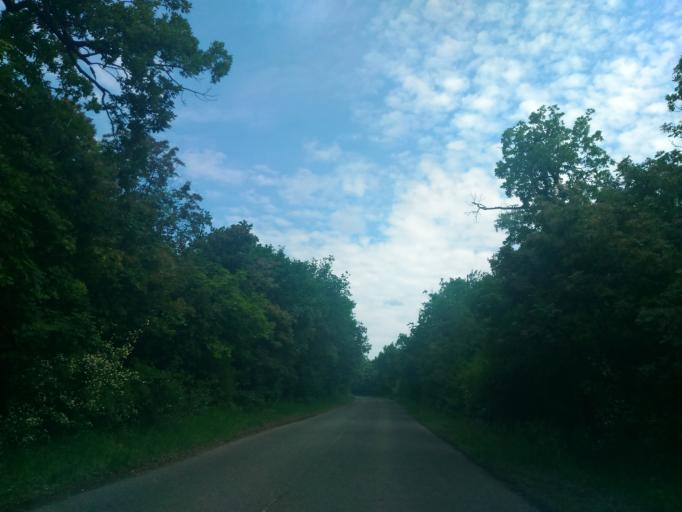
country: HU
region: Baranya
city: Pecs
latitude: 46.0964
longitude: 18.2276
